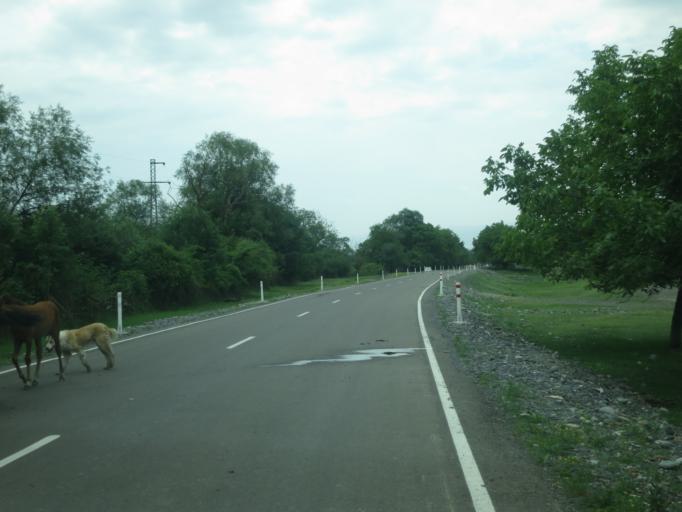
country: GE
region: Kakheti
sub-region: Telavi
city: Telavi
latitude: 42.1240
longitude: 45.4247
